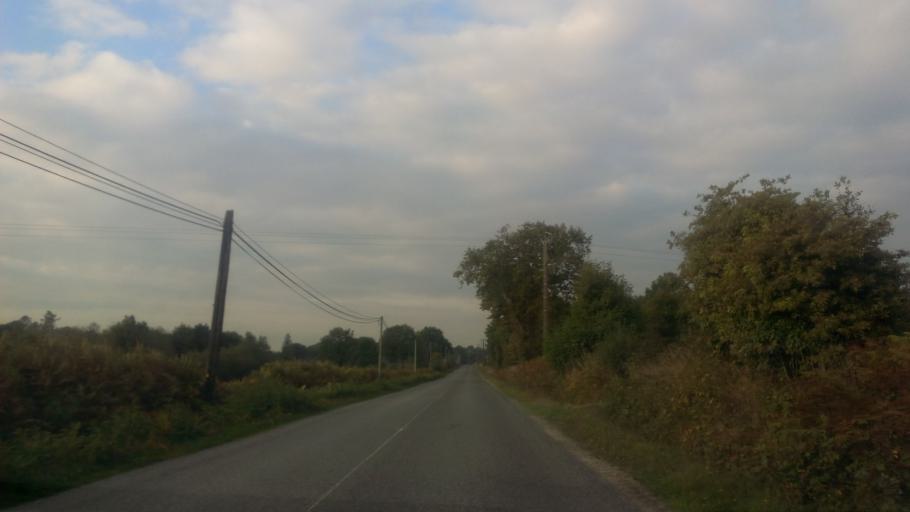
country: FR
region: Brittany
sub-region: Departement du Morbihan
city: Allaire
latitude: 47.6474
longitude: -2.1685
